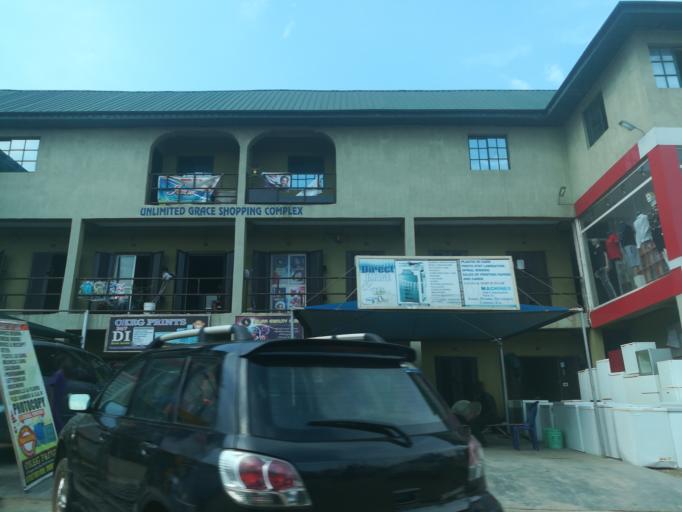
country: NG
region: Lagos
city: Ikorodu
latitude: 6.6241
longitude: 3.5045
